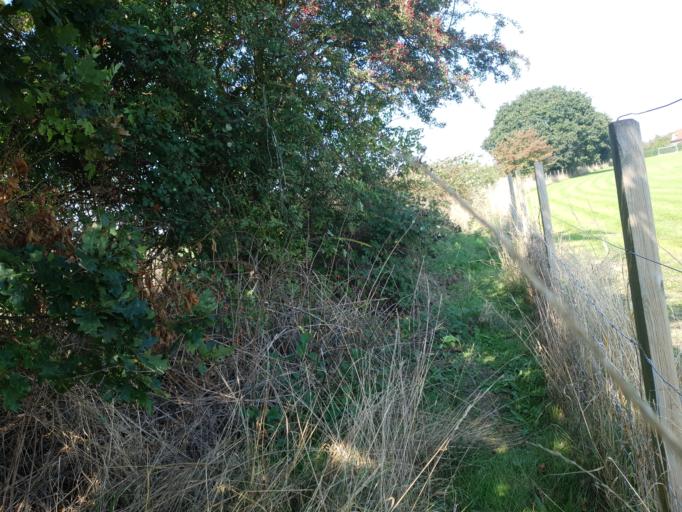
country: GB
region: England
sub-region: Suffolk
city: East Bergholt
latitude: 51.9310
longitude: 0.9902
